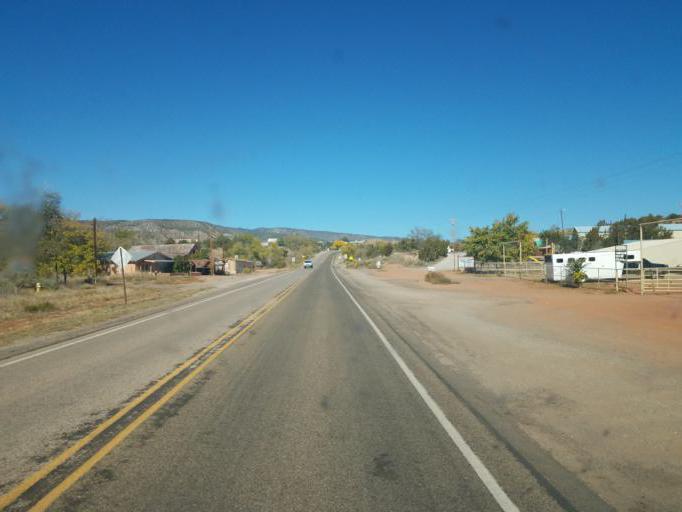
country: US
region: New Mexico
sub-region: Sandoval County
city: Jemez Pueblo
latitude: 35.6533
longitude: -106.7332
